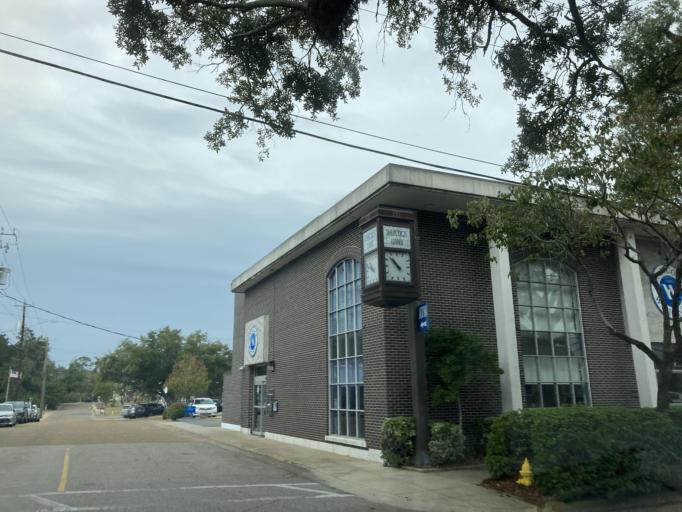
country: US
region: Mississippi
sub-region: Jackson County
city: Ocean Springs
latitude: 30.4140
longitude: -88.8278
